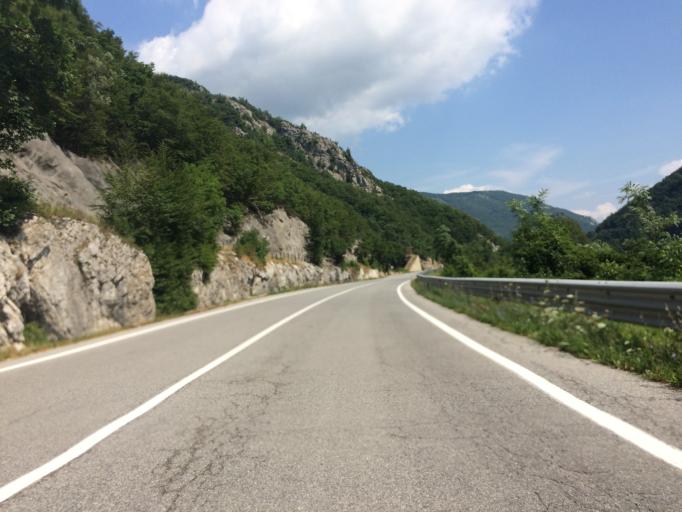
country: IT
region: Piedmont
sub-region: Provincia di Cuneo
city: Ormea
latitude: 44.1725
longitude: 7.9771
